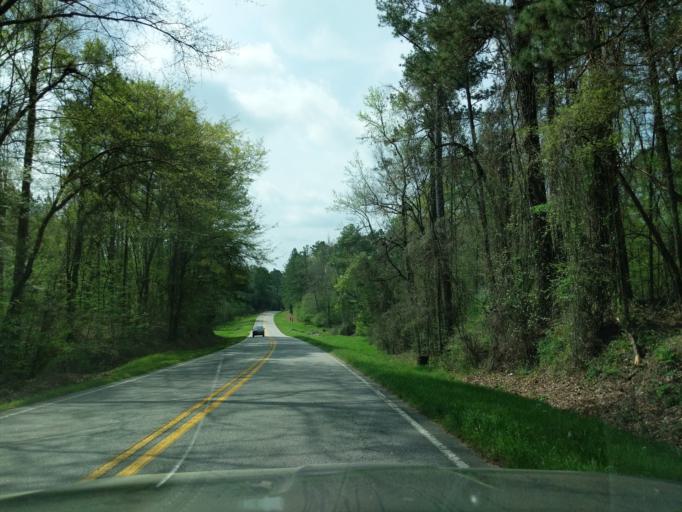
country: US
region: Georgia
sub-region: Columbia County
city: Appling
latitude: 33.5798
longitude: -82.3180
